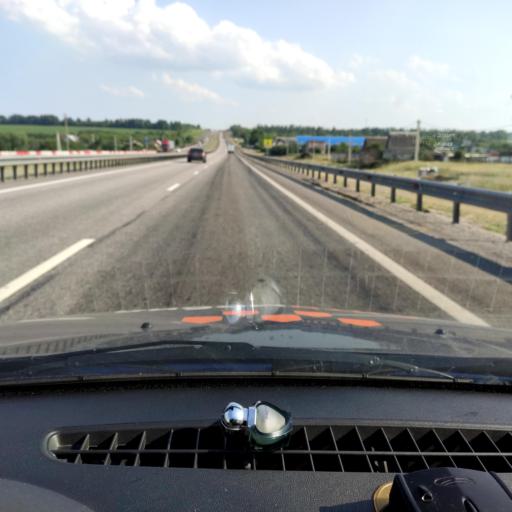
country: RU
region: Voronezj
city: Ramon'
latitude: 52.0395
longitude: 39.1979
